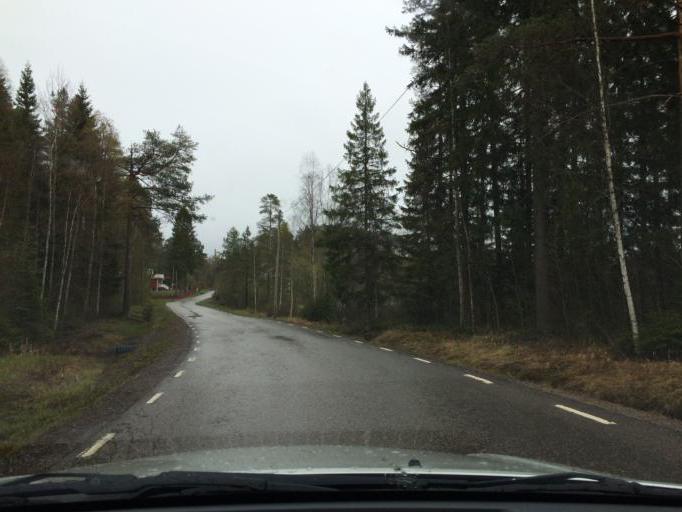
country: SE
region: Dalarna
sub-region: Ludvika Kommun
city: Abborrberget
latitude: 60.0445
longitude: 14.7644
